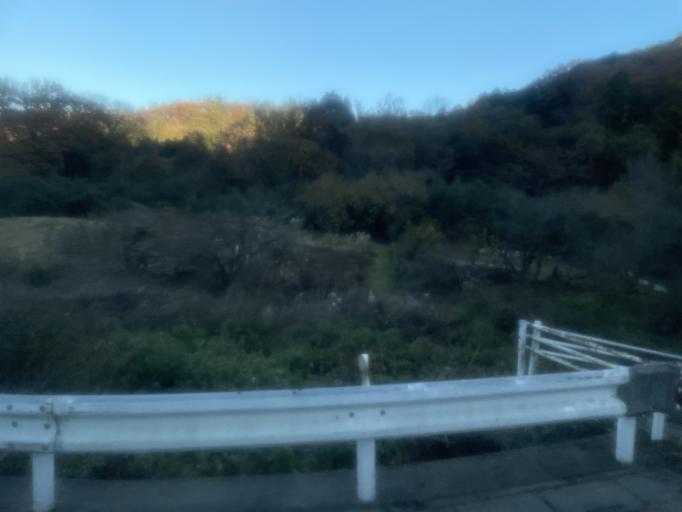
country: JP
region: Saitama
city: Yorii
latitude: 36.0939
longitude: 139.1745
